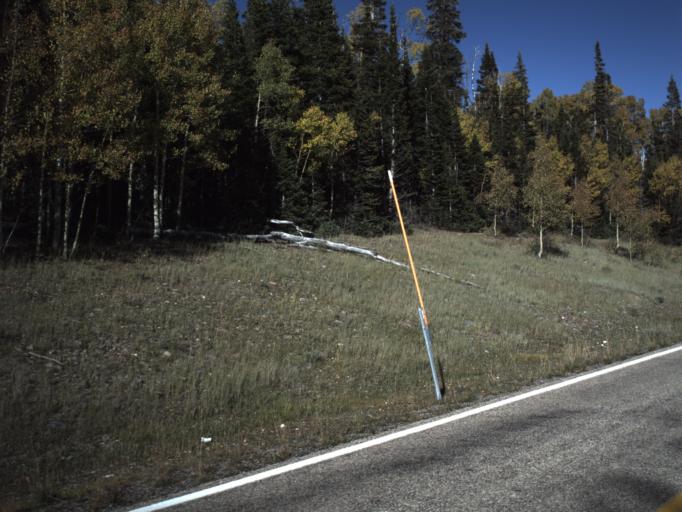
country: US
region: Utah
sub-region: Iron County
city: Parowan
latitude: 37.6585
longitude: -112.7476
